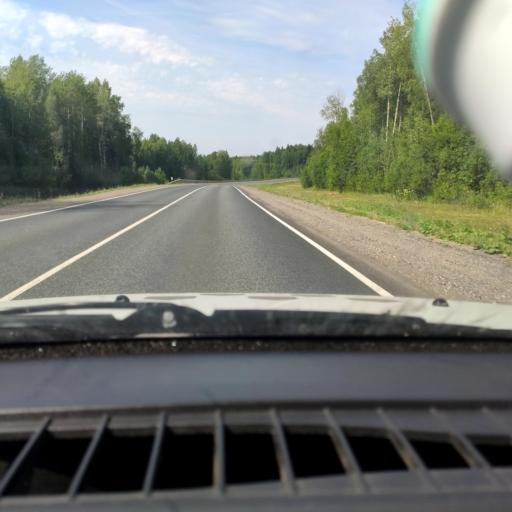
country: RU
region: Kirov
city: Kostino
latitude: 58.7494
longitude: 53.6120
